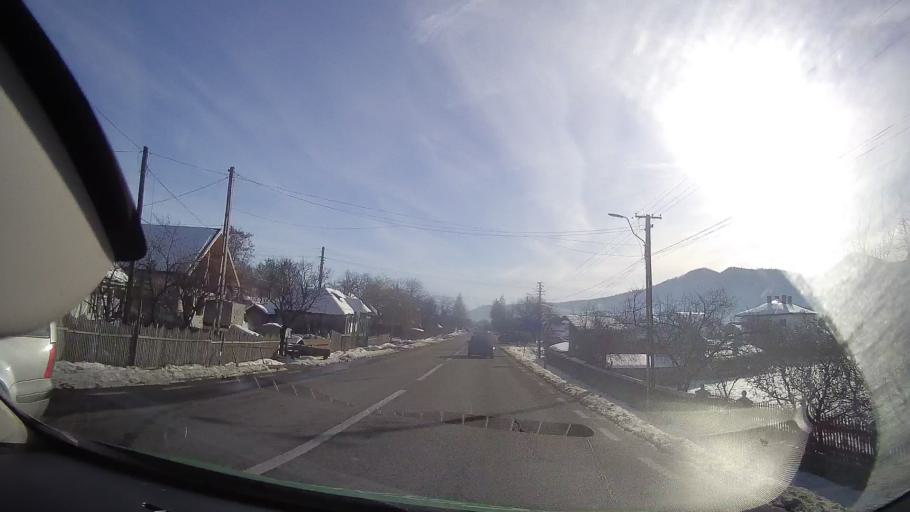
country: RO
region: Neamt
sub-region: Comuna Cracaoani
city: Cracaoani
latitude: 47.1005
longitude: 26.3085
